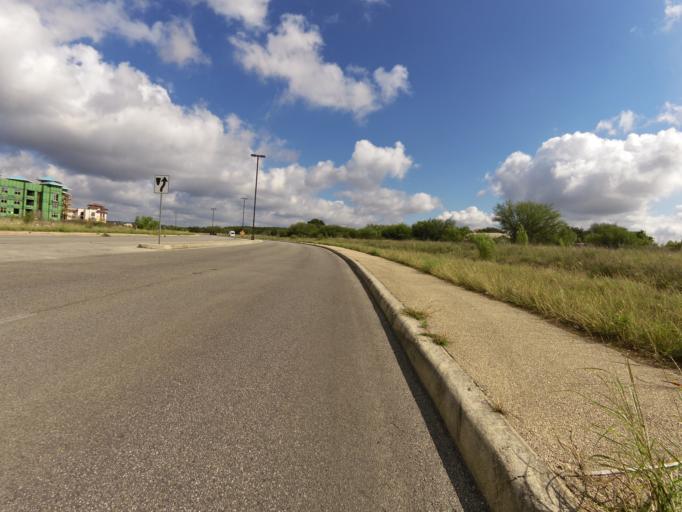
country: US
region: Texas
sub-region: Bexar County
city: Shavano Park
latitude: 29.5950
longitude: -98.5894
